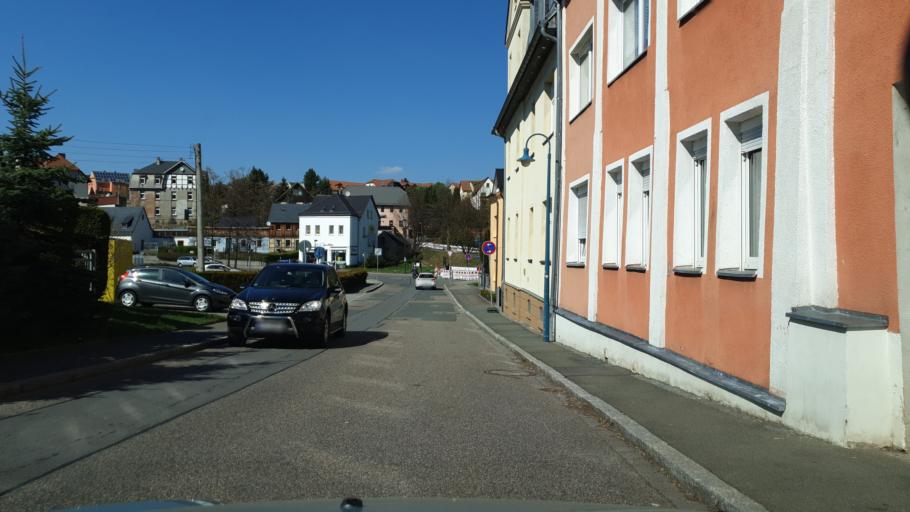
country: DE
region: Saxony
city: Oelsnitz
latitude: 50.7233
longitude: 12.7052
